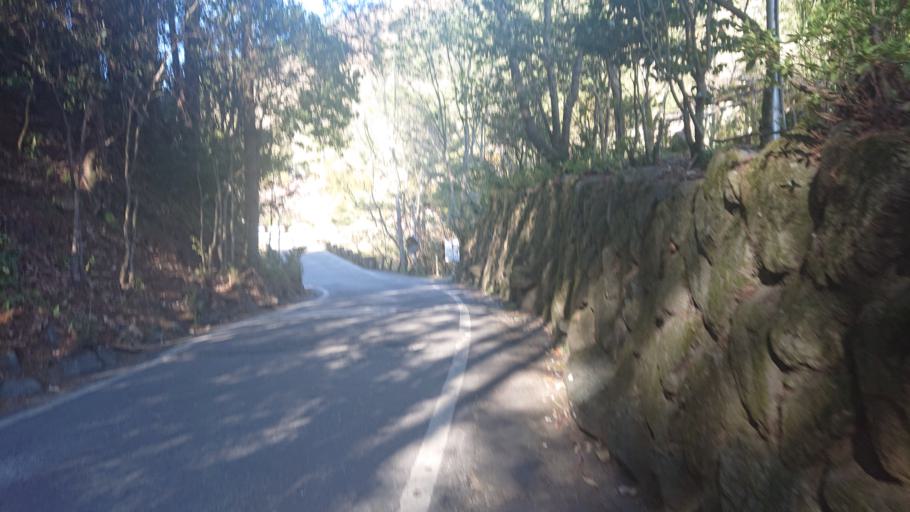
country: TW
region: Taiwan
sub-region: Hualien
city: Hualian
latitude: 24.3557
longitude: 121.3123
